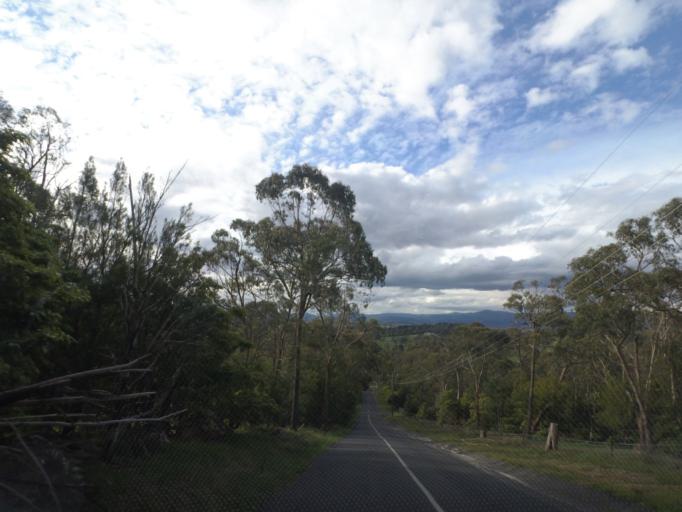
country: AU
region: Victoria
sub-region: Yarra Ranges
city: Mount Evelyn
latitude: -37.7506
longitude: 145.4111
